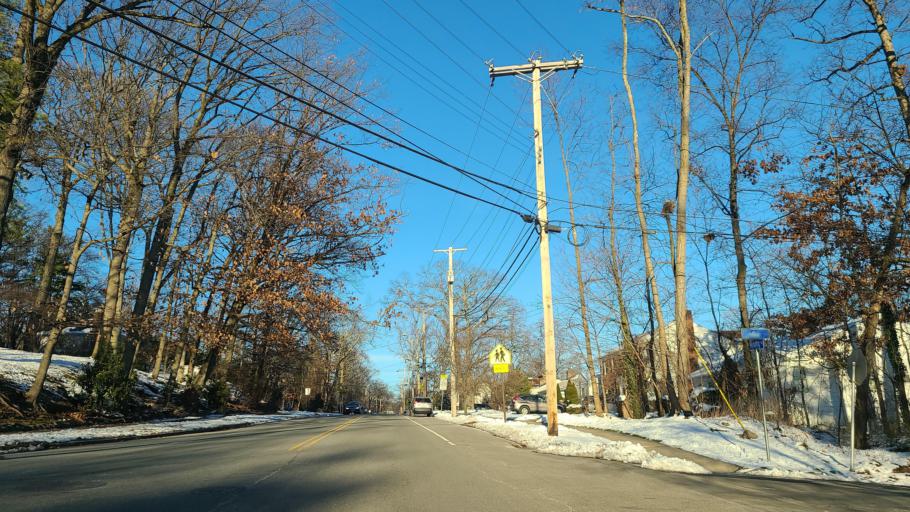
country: US
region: New Jersey
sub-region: Essex County
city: Maplewood
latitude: 40.7273
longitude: -74.2938
